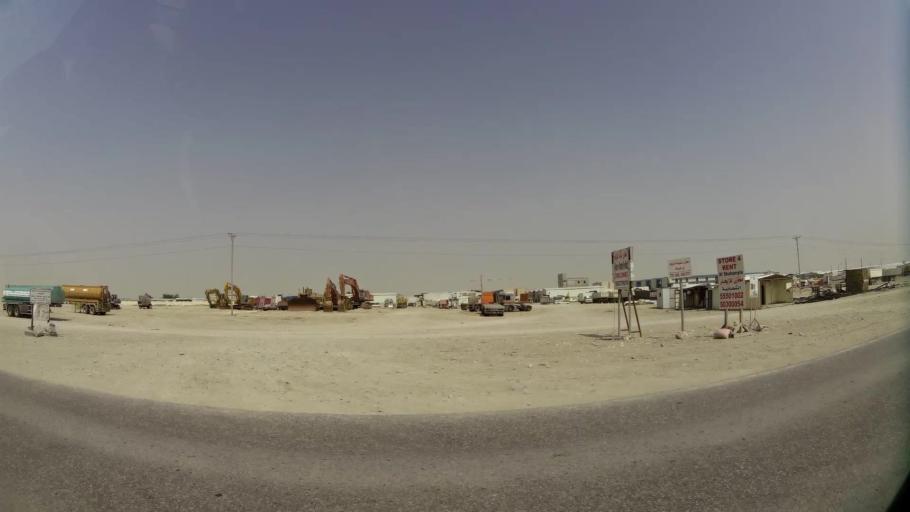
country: QA
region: Baladiyat ar Rayyan
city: Ar Rayyan
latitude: 25.2144
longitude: 51.3569
